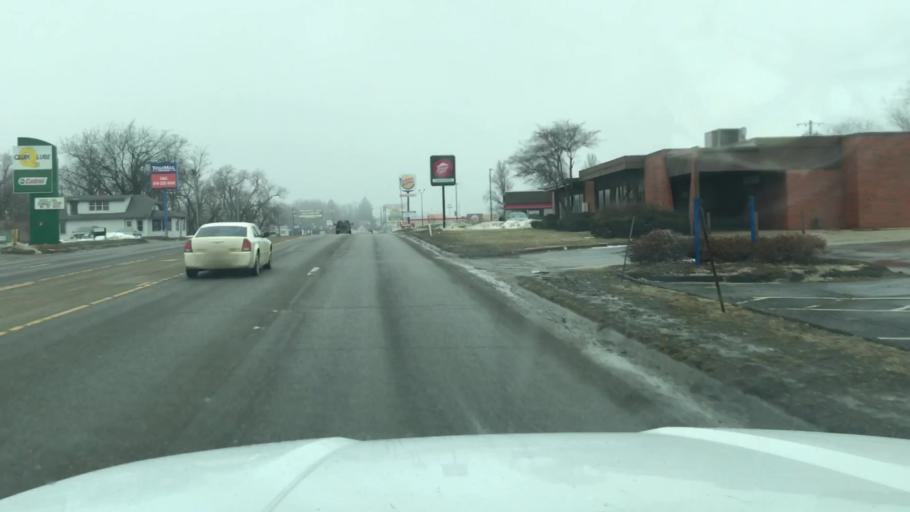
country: US
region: Missouri
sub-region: Buchanan County
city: Saint Joseph
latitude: 39.7510
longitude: -94.8029
